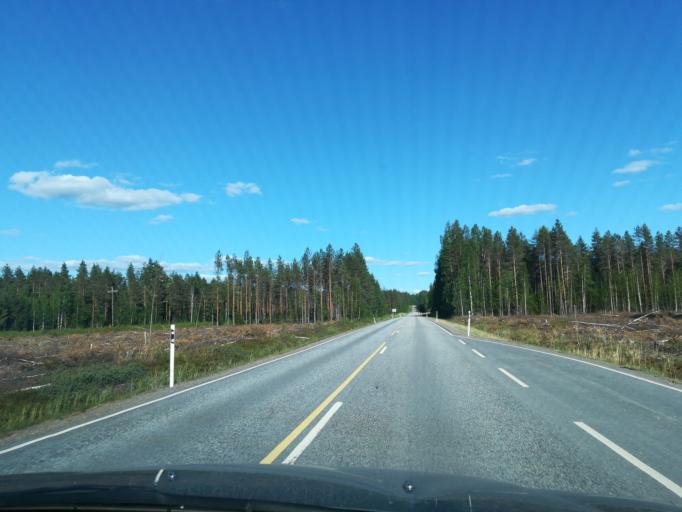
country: FI
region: South Karelia
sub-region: Imatra
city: Ruokolahti
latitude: 61.4037
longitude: 28.5785
